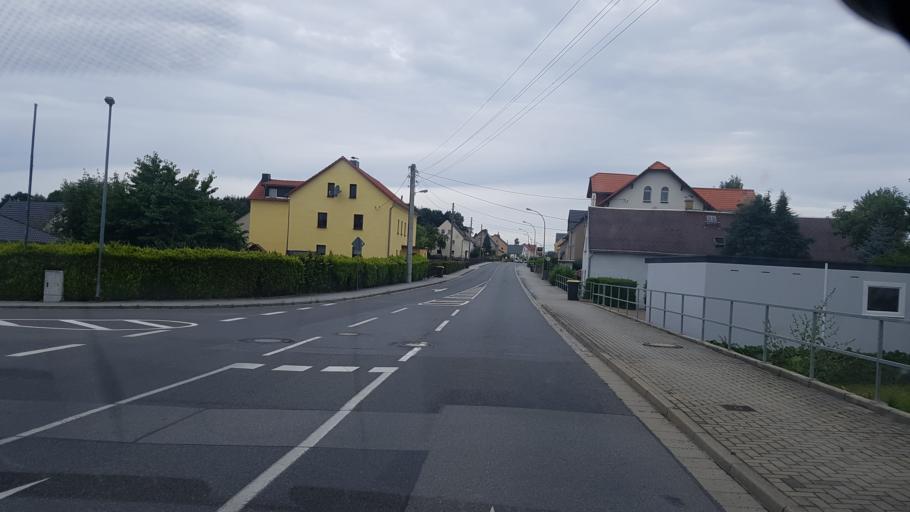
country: DE
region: Saxony
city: Ohorn
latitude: 51.1677
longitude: 14.0482
